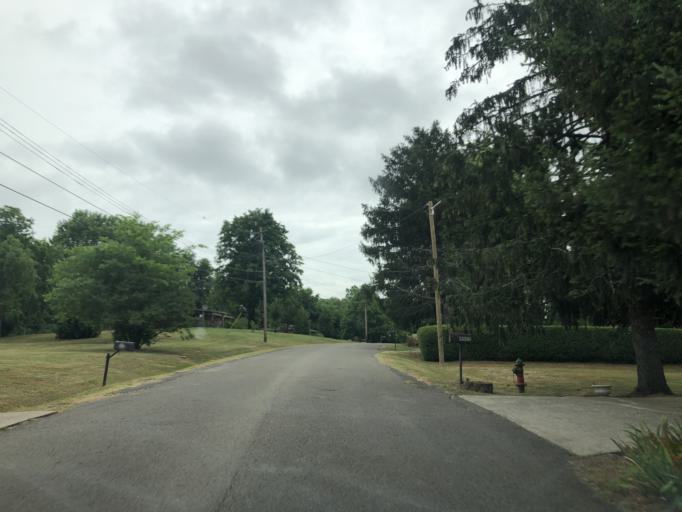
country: US
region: Tennessee
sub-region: Davidson County
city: Goodlettsville
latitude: 36.2681
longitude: -86.7745
